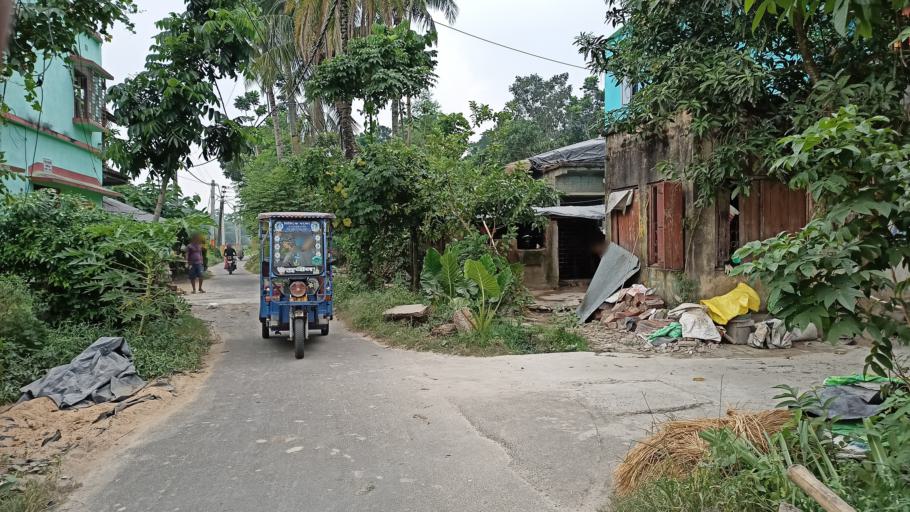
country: IN
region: West Bengal
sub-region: North 24 Parganas
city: Bangaon
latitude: 23.0642
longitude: 88.8187
